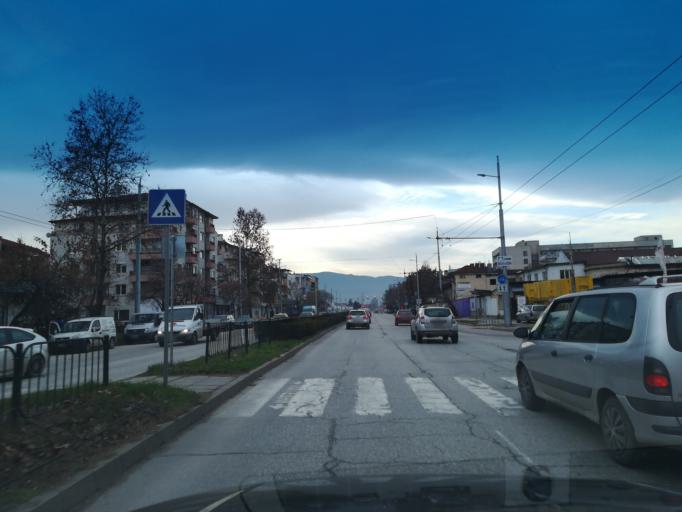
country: BG
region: Plovdiv
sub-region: Obshtina Plovdiv
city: Plovdiv
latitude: 42.1280
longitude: 24.7218
